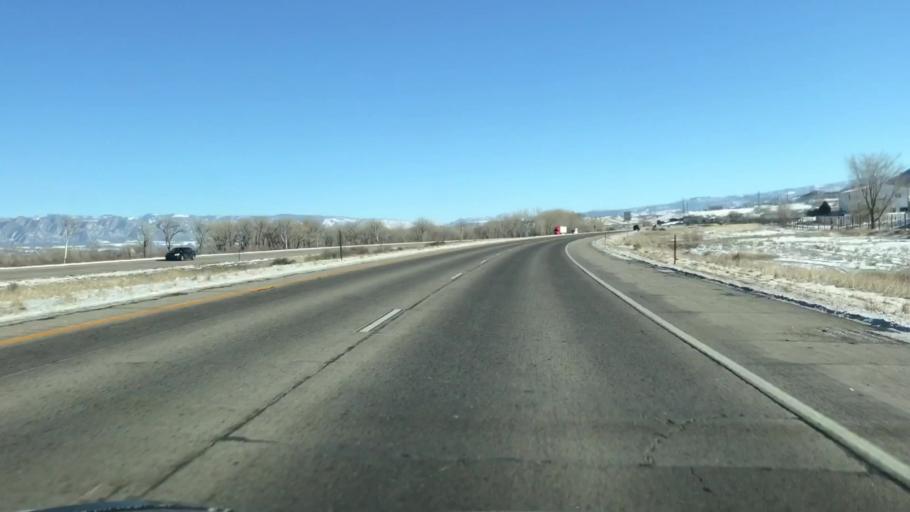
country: US
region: Colorado
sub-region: Garfield County
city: Rifle
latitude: 39.5261
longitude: -107.7674
